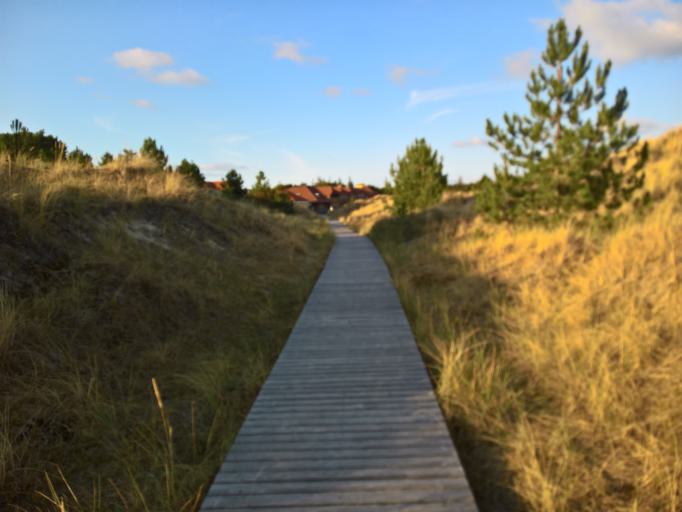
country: DE
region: Schleswig-Holstein
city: Wittdun
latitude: 54.6265
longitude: 8.3750
